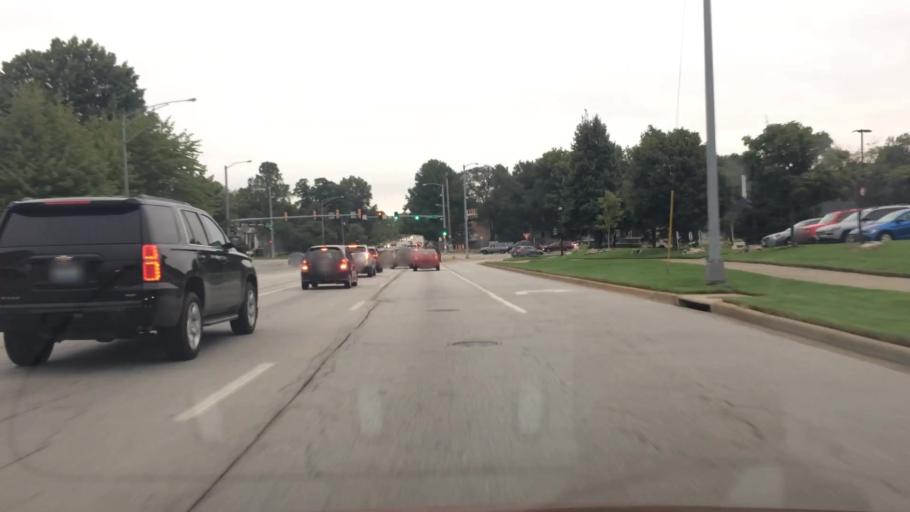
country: US
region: Missouri
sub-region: Greene County
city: Springfield
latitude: 37.1806
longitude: -93.2766
